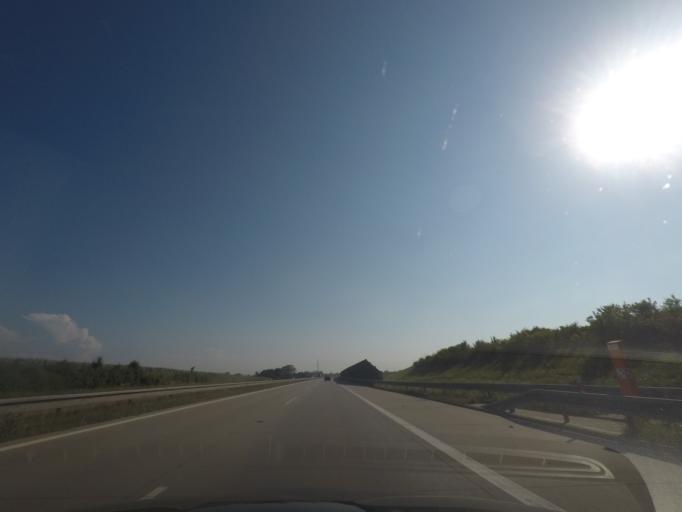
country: CZ
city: Bilovec
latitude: 49.7156
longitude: 18.0034
